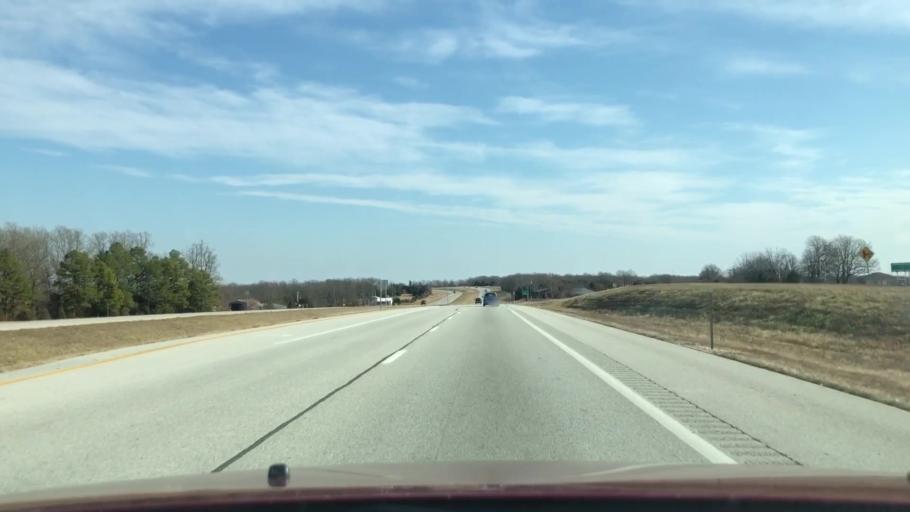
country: US
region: Missouri
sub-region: Webster County
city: Seymour
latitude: 37.1631
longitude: -92.8845
